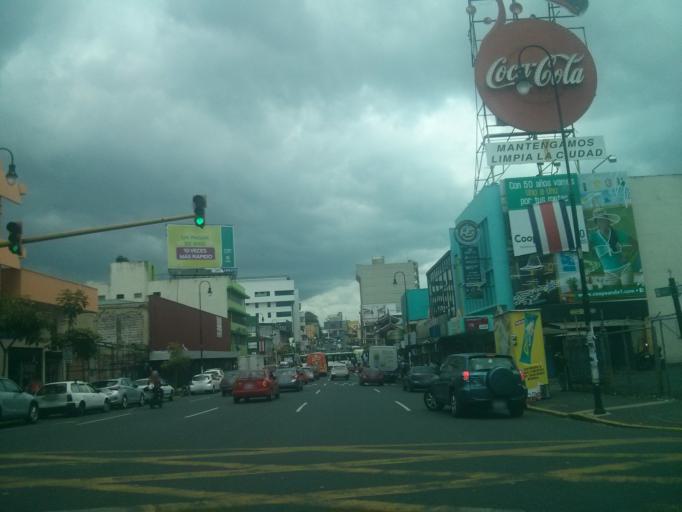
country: CR
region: San Jose
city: San Jose
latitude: 9.9326
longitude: -84.0757
